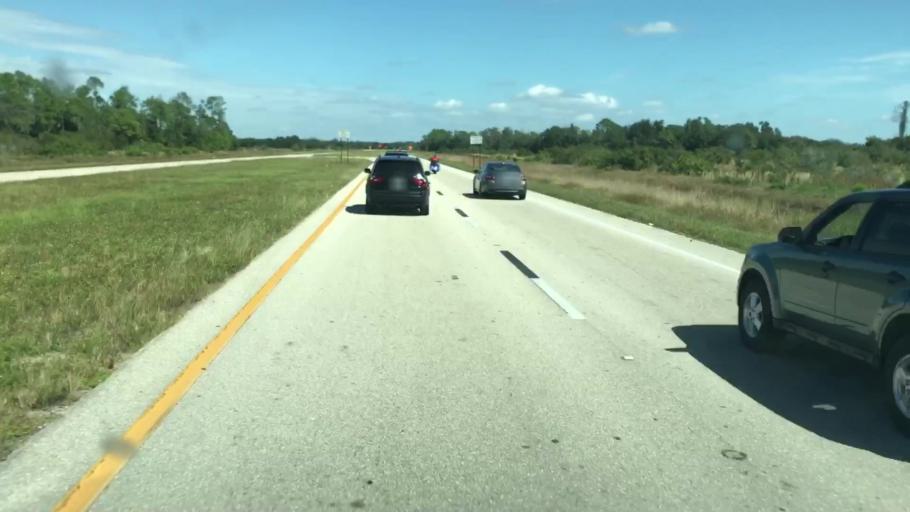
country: US
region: Florida
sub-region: Lee County
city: Gateway
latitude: 26.5691
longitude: -81.7281
